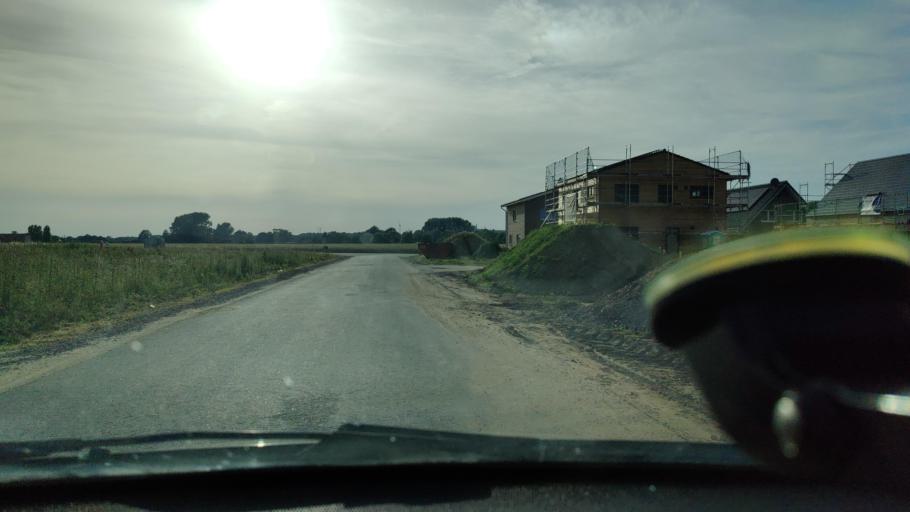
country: DE
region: North Rhine-Westphalia
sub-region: Regierungsbezirk Munster
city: Billerbeck
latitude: 51.9781
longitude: 7.2788
